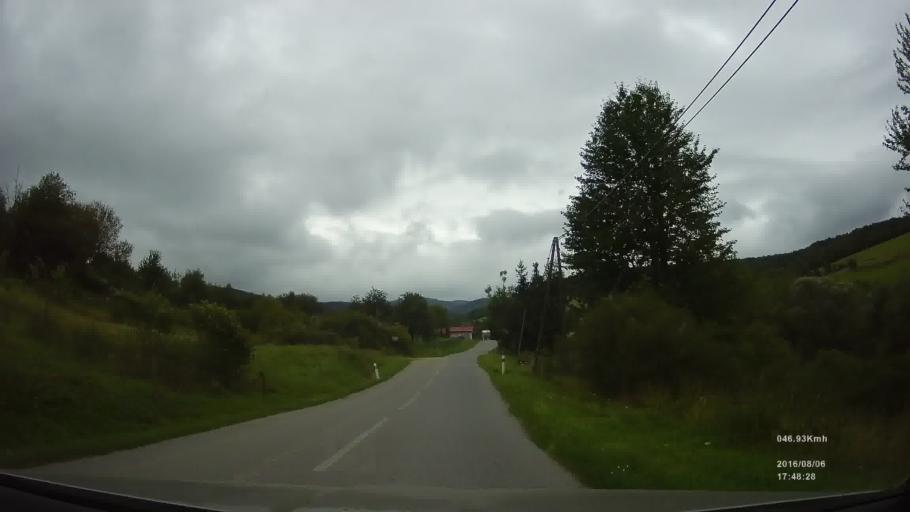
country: SK
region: Presovsky
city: Svidnik
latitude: 49.3770
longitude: 21.5731
